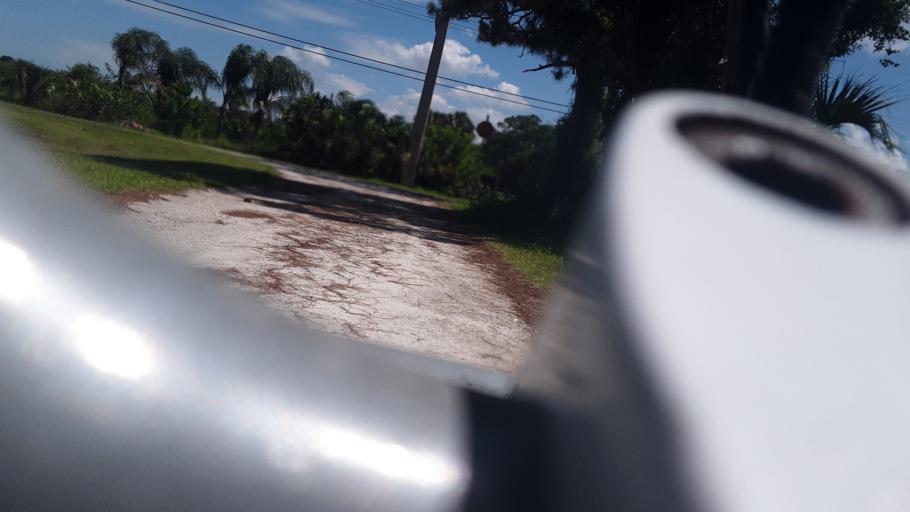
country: US
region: Florida
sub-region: Brevard County
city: Malabar
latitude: 27.9914
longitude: -80.6140
